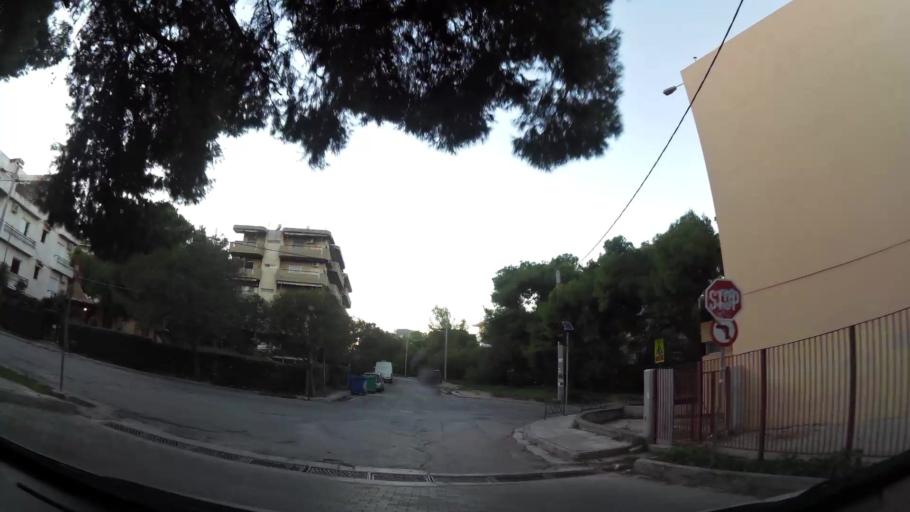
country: GR
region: Attica
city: Pefki
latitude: 38.0610
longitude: 23.7881
